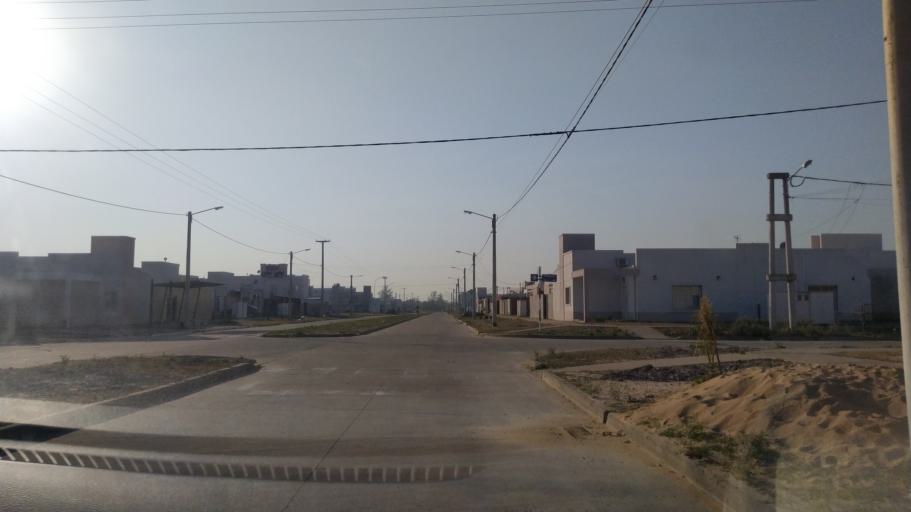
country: AR
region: Corrientes
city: Corrientes
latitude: -27.5236
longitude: -58.8070
